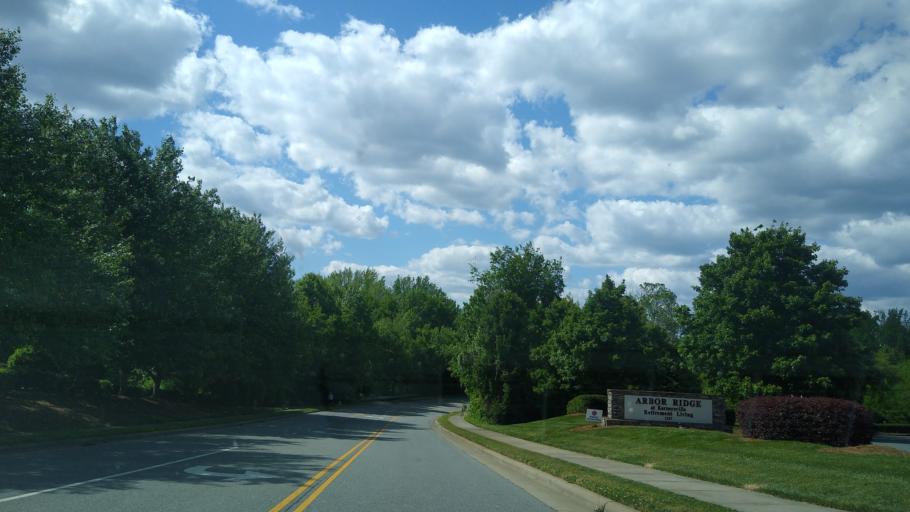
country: US
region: North Carolina
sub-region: Forsyth County
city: Kernersville
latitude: 36.1037
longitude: -80.0975
